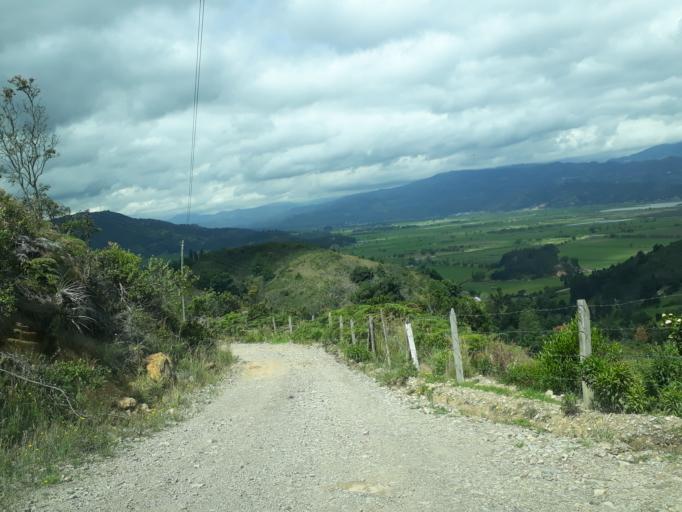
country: CO
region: Cundinamarca
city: Guacheta
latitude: 5.4404
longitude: -73.7023
